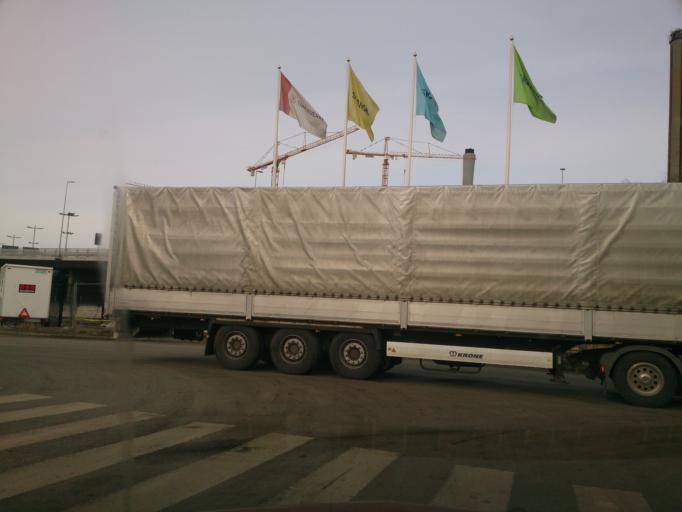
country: SE
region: Stockholm
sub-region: Stockholms Kommun
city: OEstermalm
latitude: 59.3506
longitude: 18.1061
